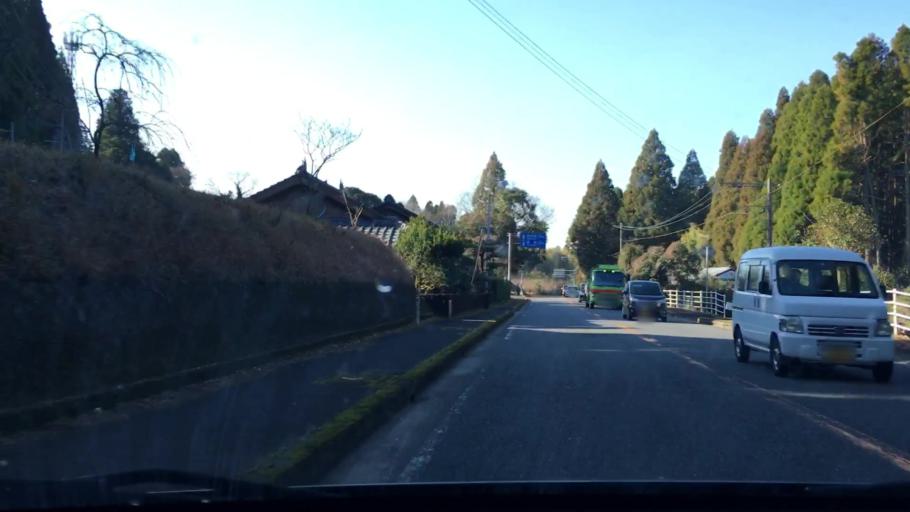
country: JP
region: Kagoshima
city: Sueyoshicho-ninokata
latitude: 31.6760
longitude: 130.9282
